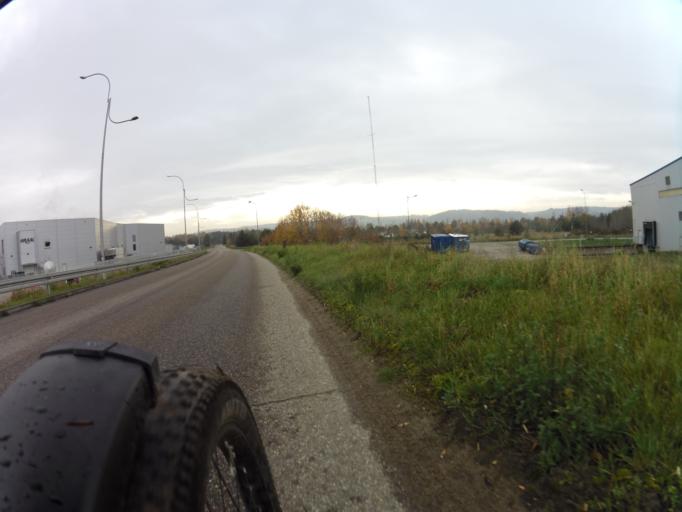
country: PL
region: Pomeranian Voivodeship
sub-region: Powiat pucki
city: Krokowa
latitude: 54.7390
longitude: 18.0945
